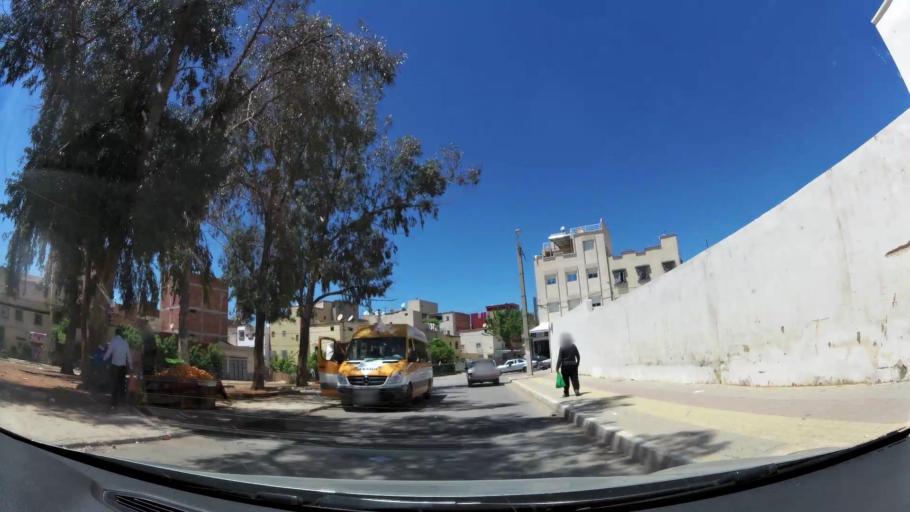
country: MA
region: Meknes-Tafilalet
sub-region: Meknes
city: Meknes
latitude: 33.9104
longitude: -5.5790
